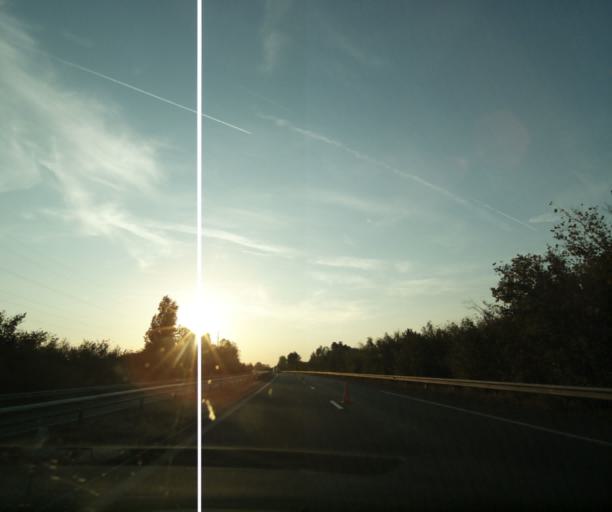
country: FR
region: Aquitaine
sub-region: Departement du Lot-et-Garonne
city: Sainte-Colombe-en-Bruilhois
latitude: 44.2109
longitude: 0.4730
